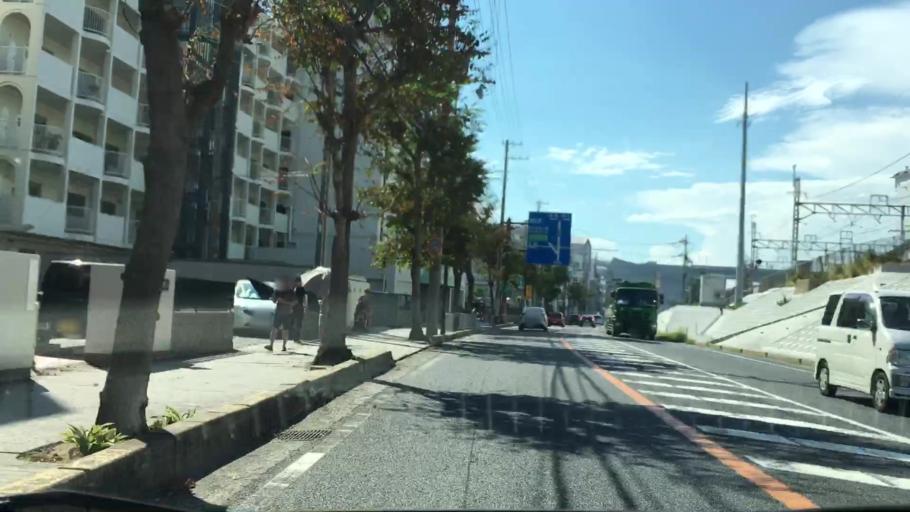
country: JP
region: Hyogo
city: Akashi
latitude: 34.6287
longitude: 135.0416
